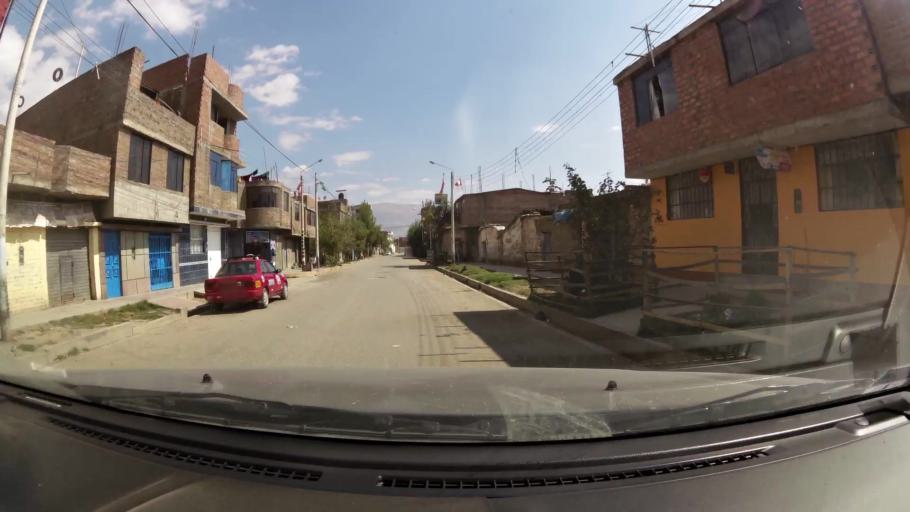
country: PE
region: Junin
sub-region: Provincia de Huancayo
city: Huancayo
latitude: -12.0878
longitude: -75.2044
